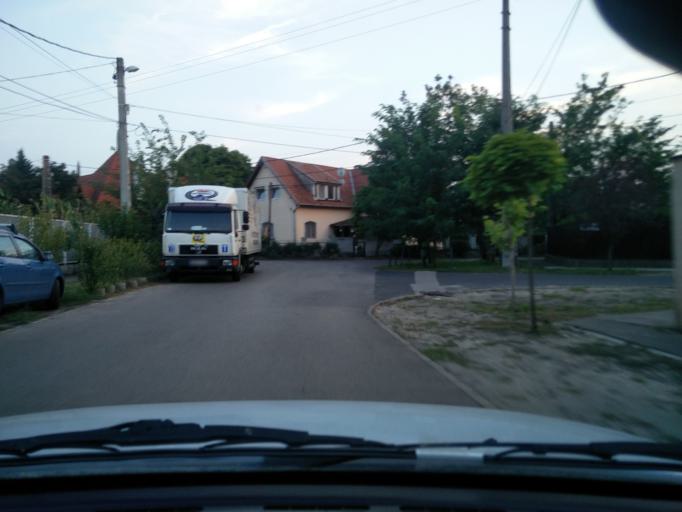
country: HU
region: Budapest
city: Budapest XXI. keruelet
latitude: 47.4134
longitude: 19.0825
